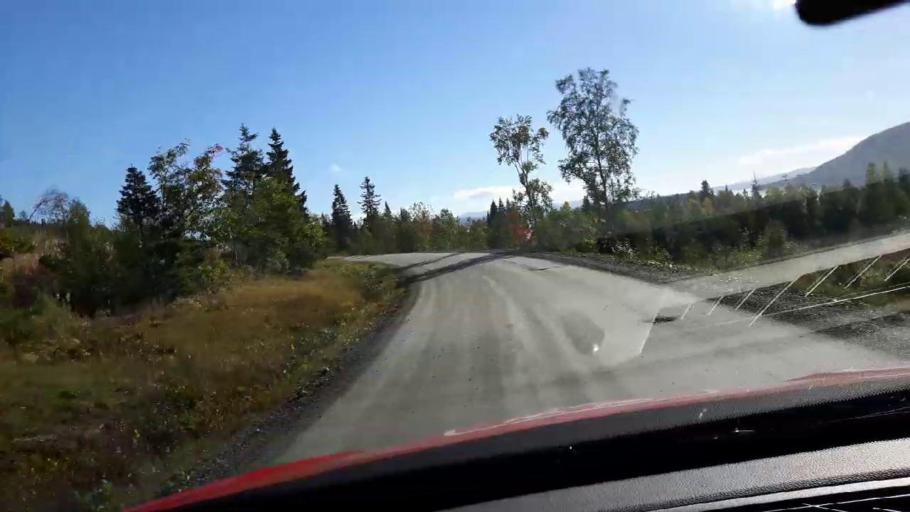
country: NO
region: Nord-Trondelag
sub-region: Lierne
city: Sandvika
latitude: 64.6421
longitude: 13.7856
